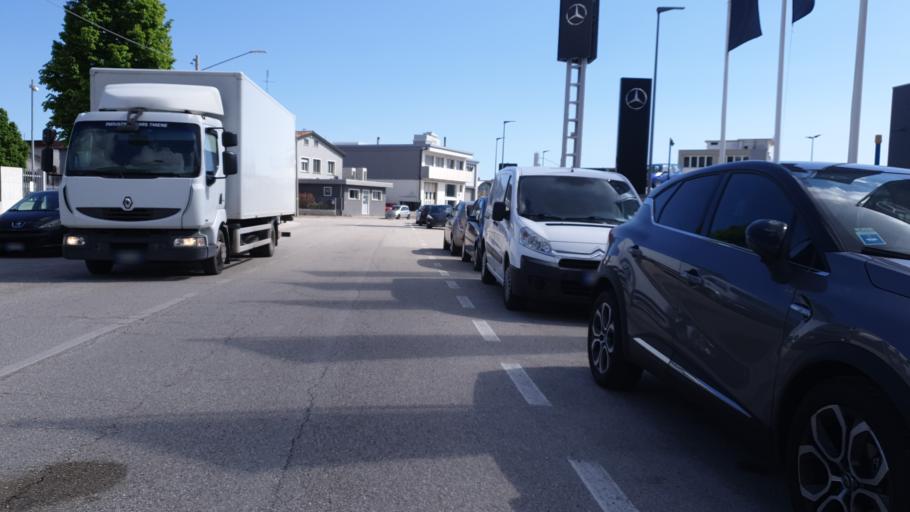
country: IT
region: Veneto
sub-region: Provincia di Padova
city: Noventa
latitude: 45.4145
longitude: 11.9301
